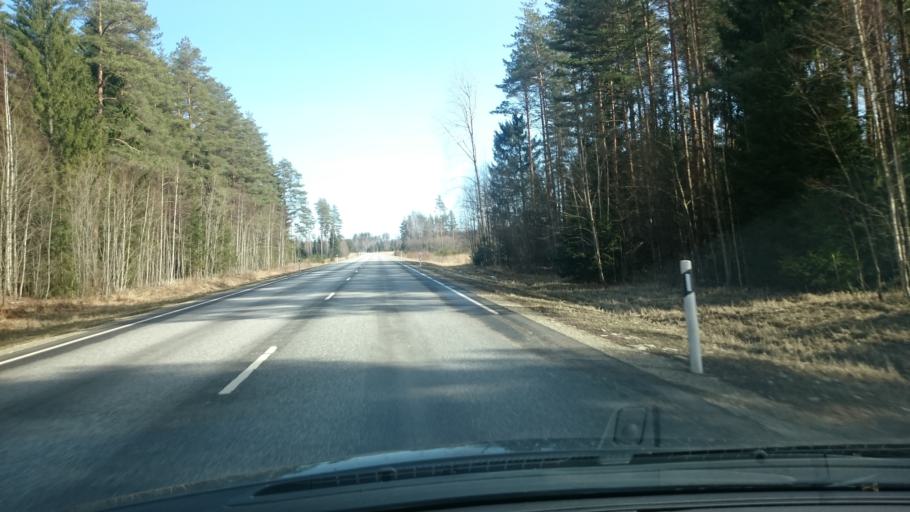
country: EE
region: Paernumaa
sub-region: Vaendra vald (alev)
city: Vandra
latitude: 58.6686
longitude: 25.1817
